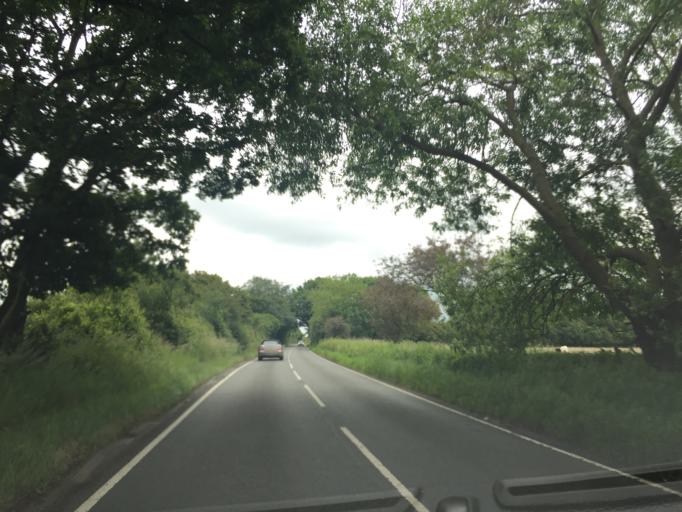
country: GB
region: England
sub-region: Essex
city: Theydon Bois
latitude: 51.6574
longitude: 0.1473
